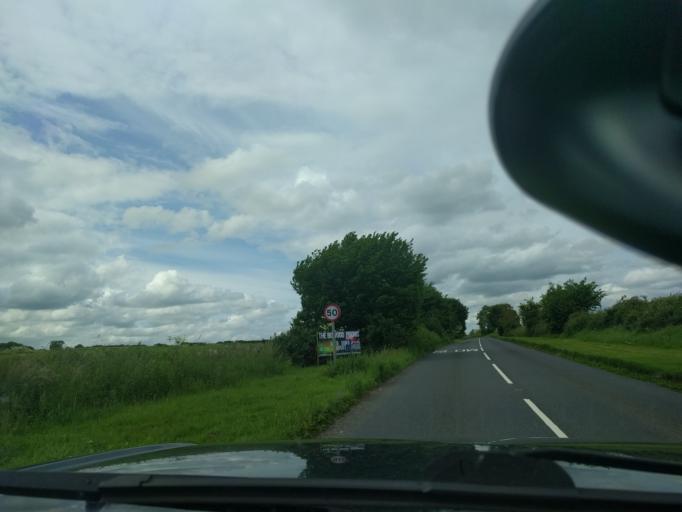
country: GB
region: England
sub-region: Wiltshire
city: Atworth
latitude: 51.4047
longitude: -2.1652
